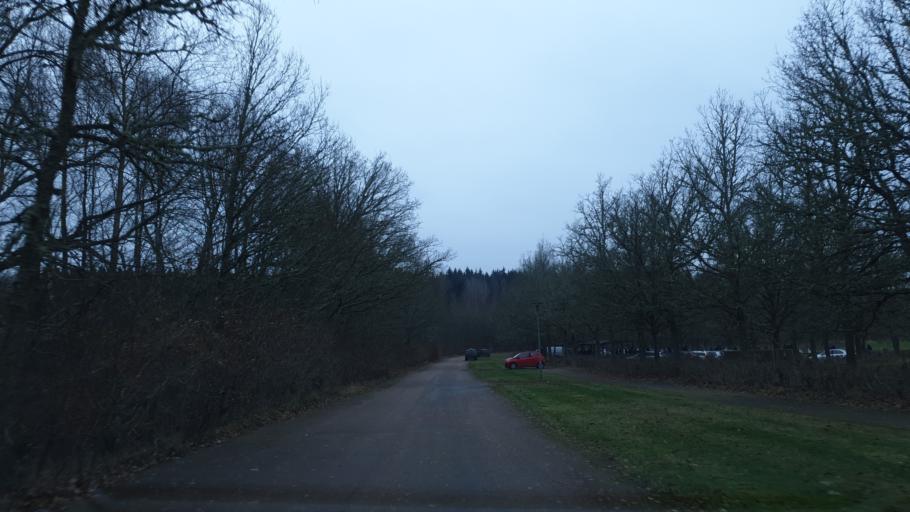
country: SE
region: Blekinge
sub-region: Karlskrona Kommun
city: Rodeby
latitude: 56.2123
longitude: 15.6824
